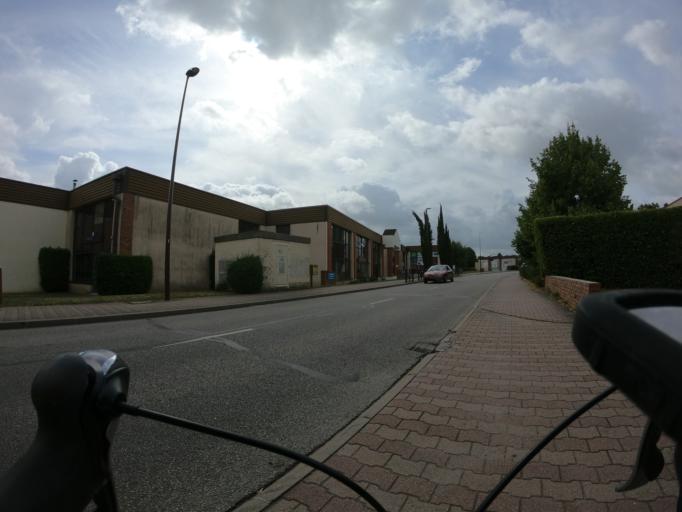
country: FR
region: Ile-de-France
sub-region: Departement des Yvelines
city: Voisins-le-Bretonneux
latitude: 48.7579
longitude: 2.0560
